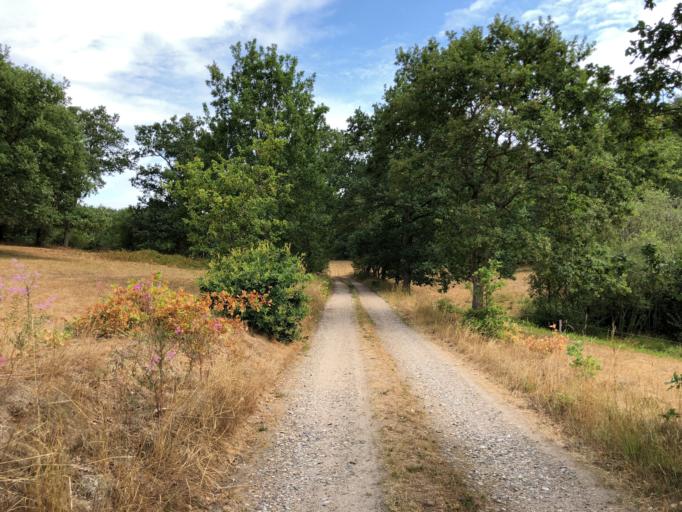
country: DK
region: South Denmark
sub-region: Vejle Kommune
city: Egtved
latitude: 55.6567
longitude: 9.2924
